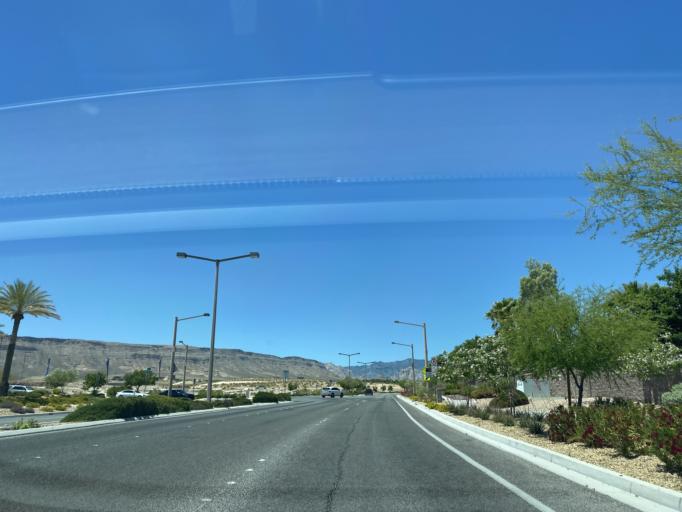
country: US
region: Nevada
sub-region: Clark County
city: Summerlin South
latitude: 36.1000
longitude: -115.3234
